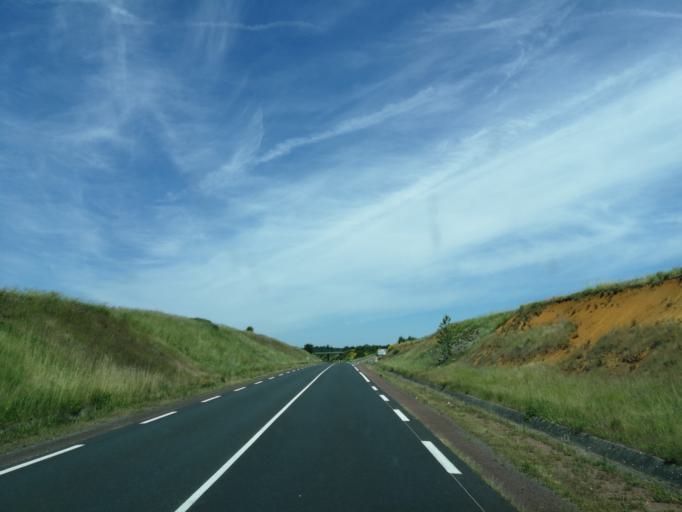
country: FR
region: Pays de la Loire
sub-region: Departement de la Vendee
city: Pissotte
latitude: 46.4986
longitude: -0.8245
